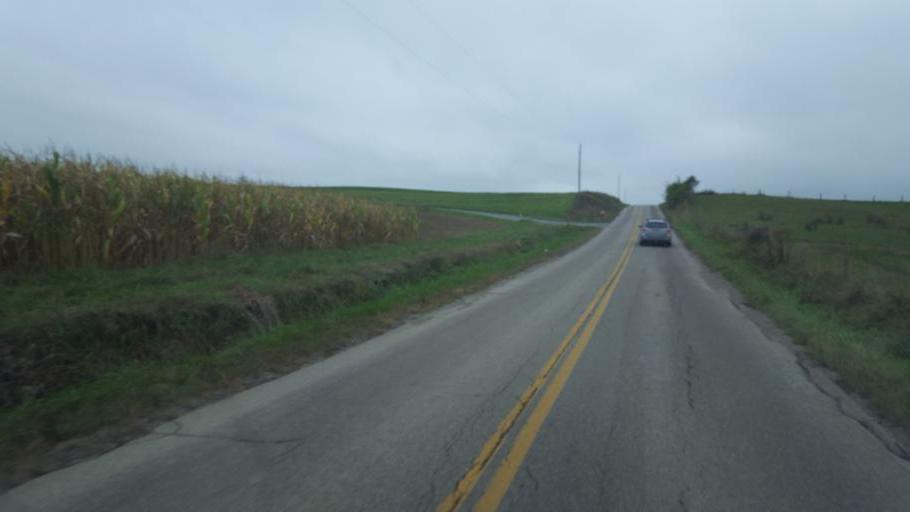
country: US
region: Ohio
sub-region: Wayne County
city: Apple Creek
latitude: 40.6580
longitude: -81.7842
